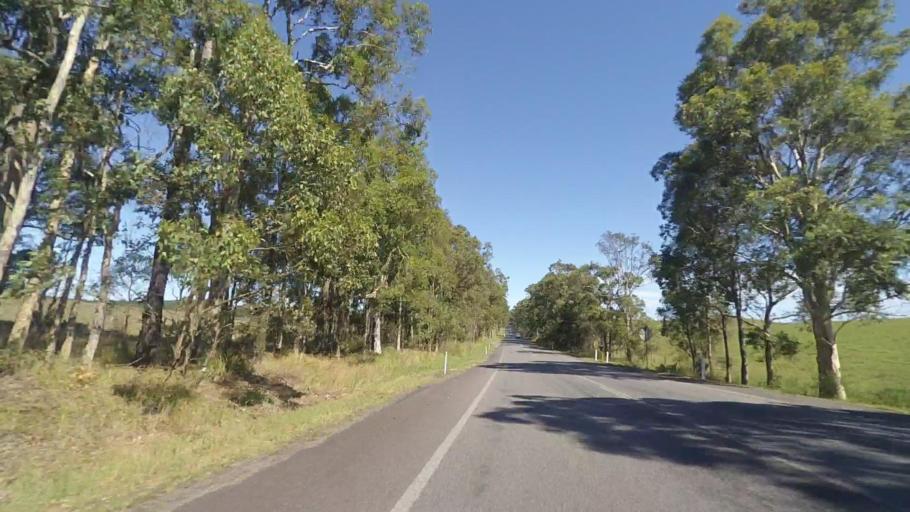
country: AU
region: New South Wales
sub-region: Great Lakes
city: Hawks Nest
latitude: -32.6286
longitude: 152.1336
